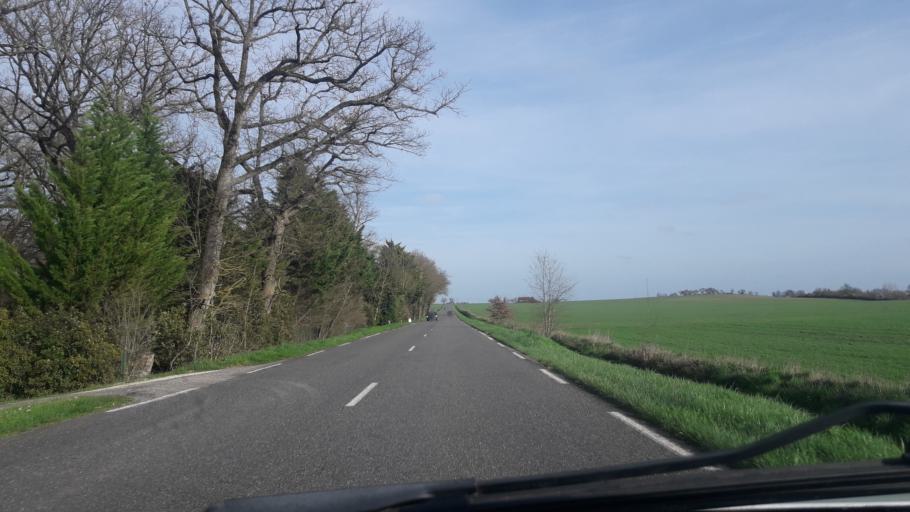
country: FR
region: Midi-Pyrenees
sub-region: Departement du Gers
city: Gimont
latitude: 43.7237
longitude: 0.9234
